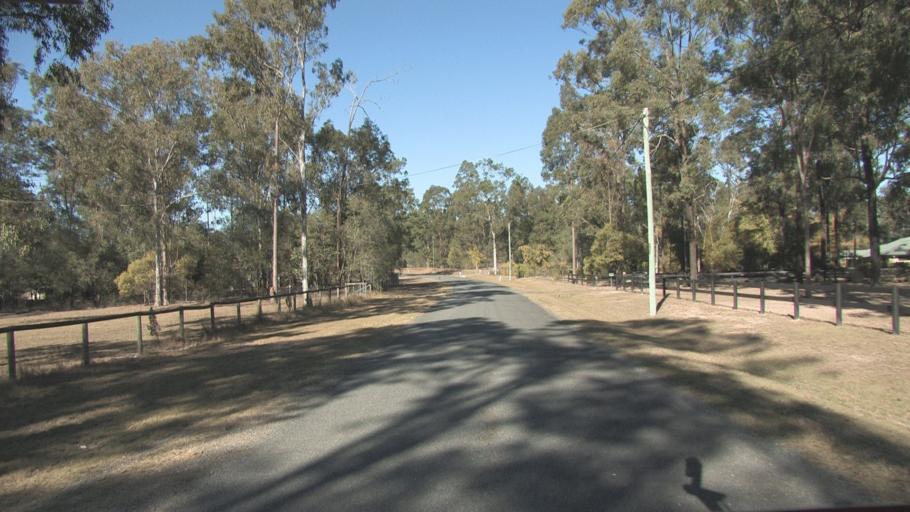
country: AU
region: Queensland
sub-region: Logan
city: North Maclean
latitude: -27.8098
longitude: 152.9711
